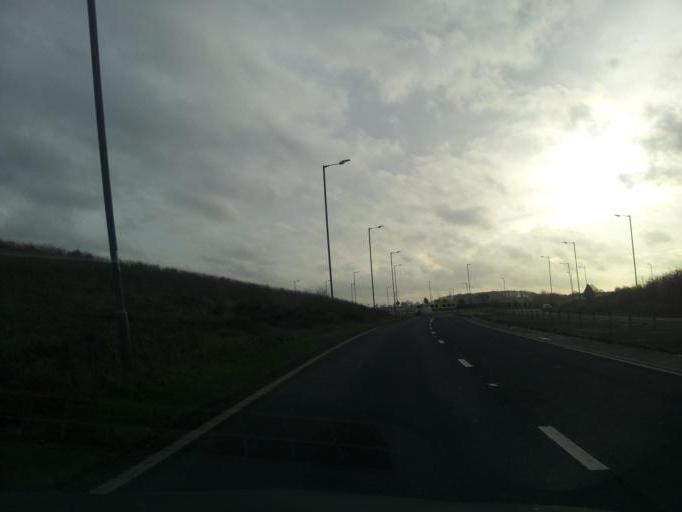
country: GB
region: England
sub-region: Central Bedfordshire
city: Leighton Buzzard
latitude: 51.9286
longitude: -0.6963
